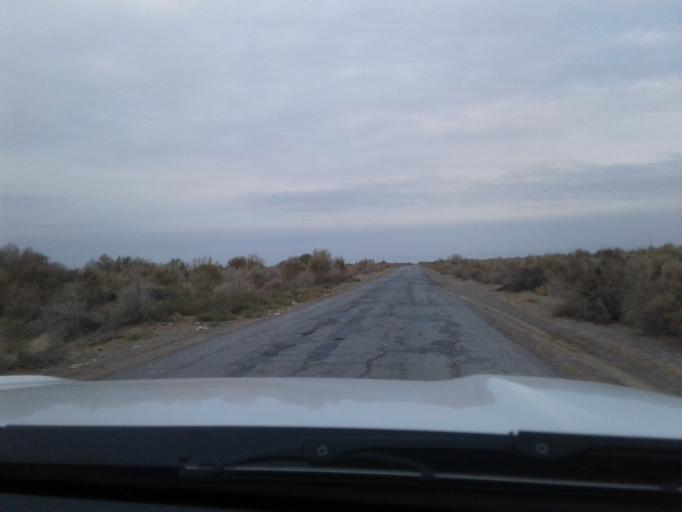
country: TM
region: Mary
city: Mary
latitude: 38.0562
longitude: 61.8346
